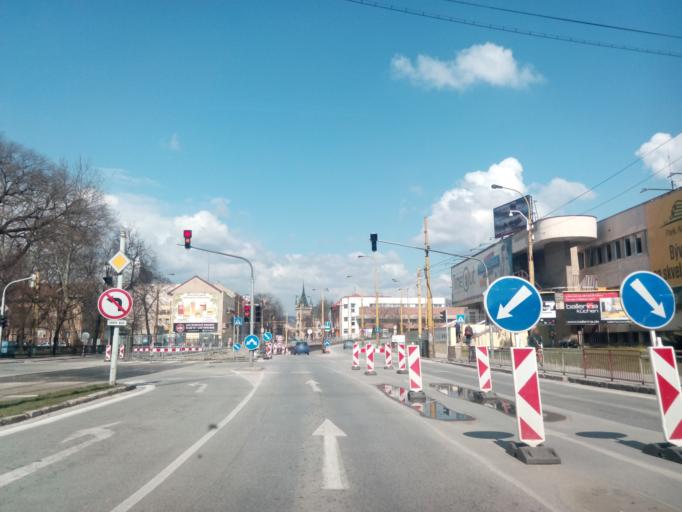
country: SK
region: Kosicky
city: Kosice
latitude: 48.7192
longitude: 21.2648
